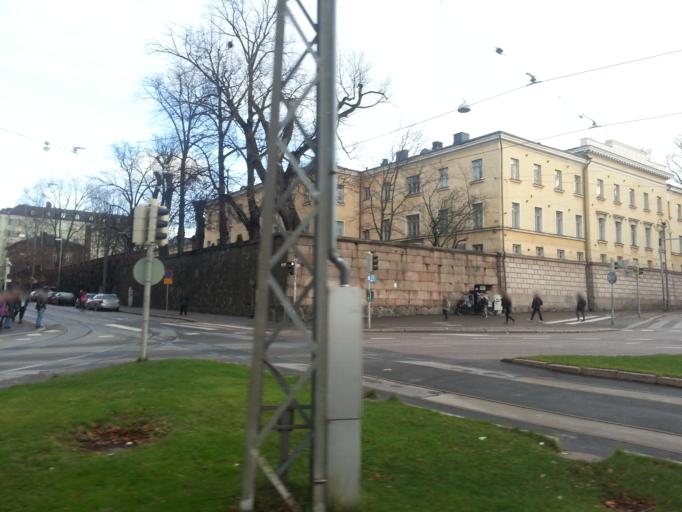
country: FI
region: Uusimaa
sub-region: Helsinki
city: Helsinki
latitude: 60.1741
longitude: 24.9501
